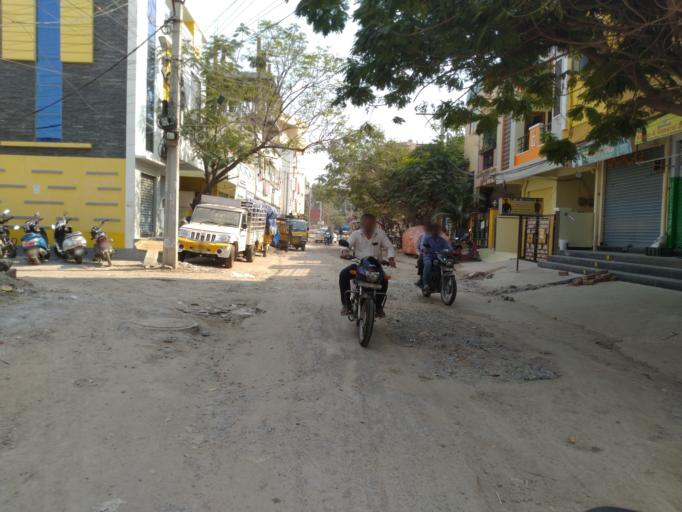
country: IN
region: Telangana
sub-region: Rangareddi
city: Quthbullapur
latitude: 17.4966
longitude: 78.4646
